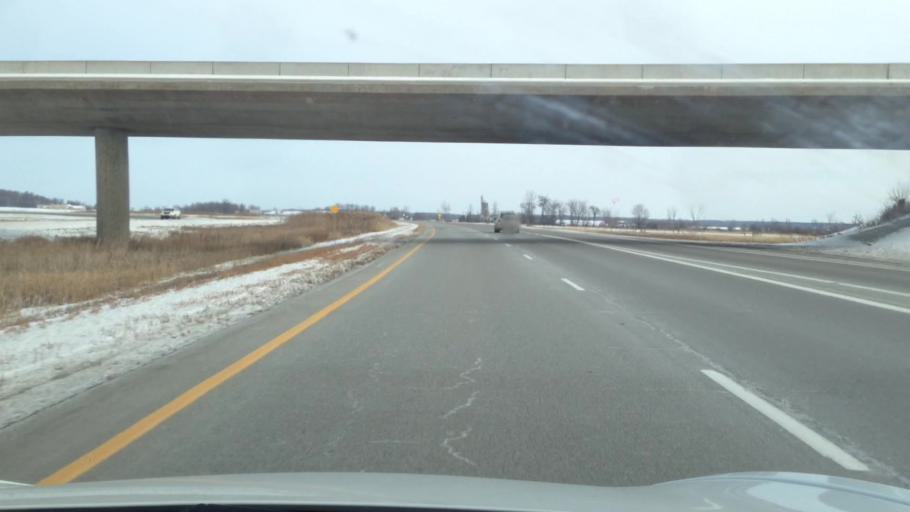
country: CA
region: Ontario
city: Casselman
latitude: 45.3431
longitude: -74.8992
